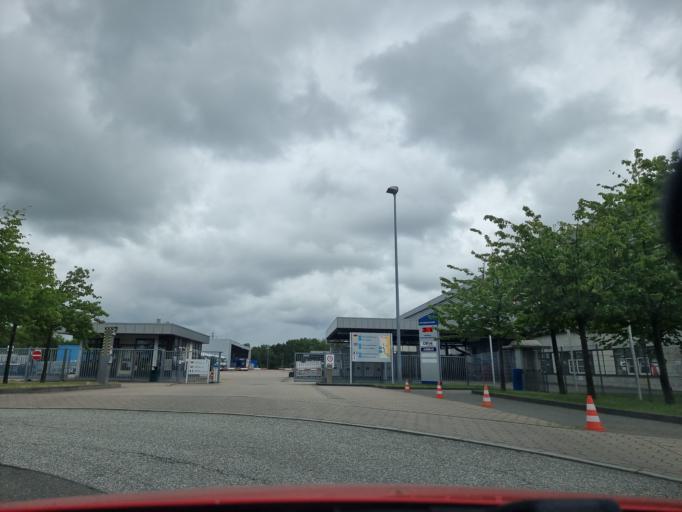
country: DE
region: Hamburg
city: Altona
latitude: 53.4777
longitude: 9.9096
